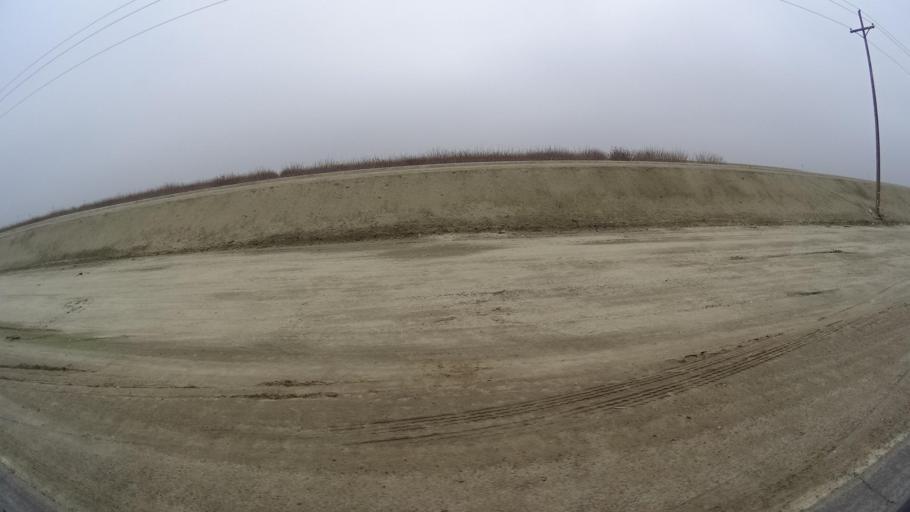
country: US
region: California
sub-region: Kern County
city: Wasco
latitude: 35.7143
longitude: -119.4016
